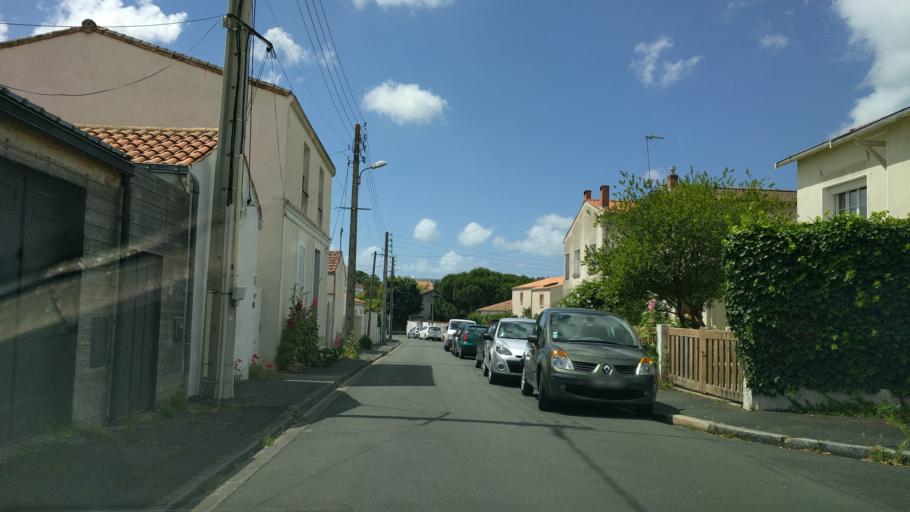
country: FR
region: Poitou-Charentes
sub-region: Departement de la Charente-Maritime
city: La Rochelle
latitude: 46.1713
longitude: -1.1441
